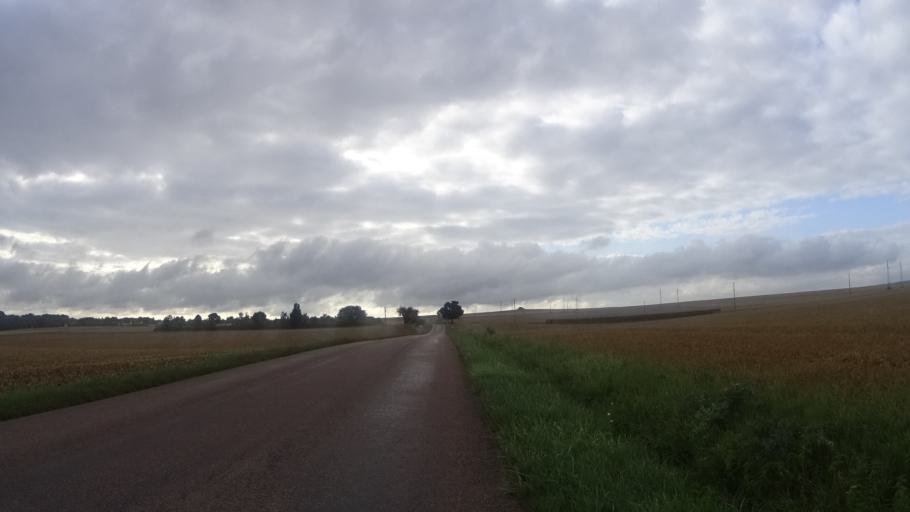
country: FR
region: Bourgogne
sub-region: Departement de l'Yonne
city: Joigny
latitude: 47.9508
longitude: 3.4187
